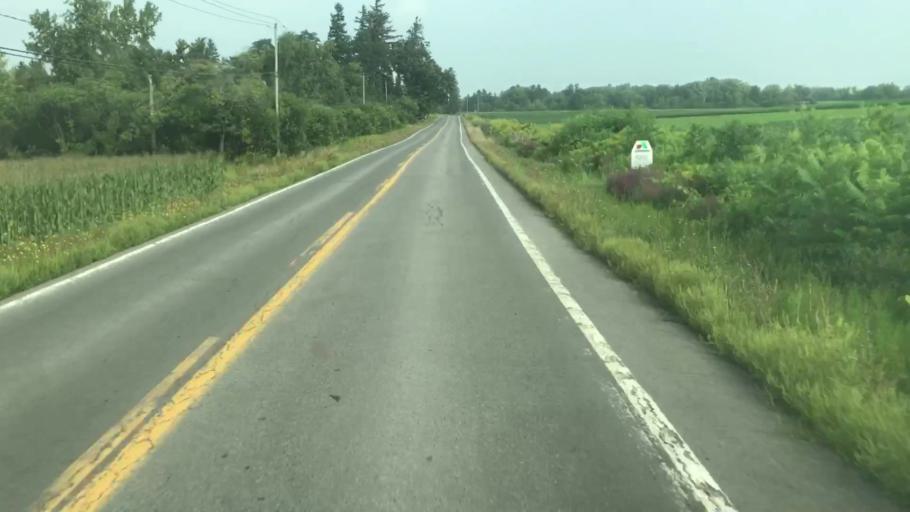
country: US
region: New York
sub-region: Onondaga County
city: Skaneateles
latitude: 42.8952
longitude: -76.4520
